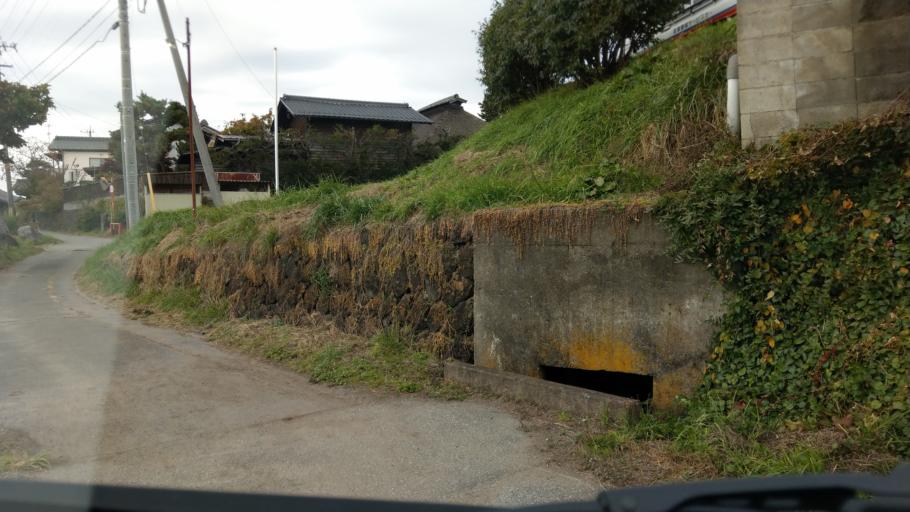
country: JP
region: Nagano
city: Komoro
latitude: 36.3217
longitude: 138.4620
